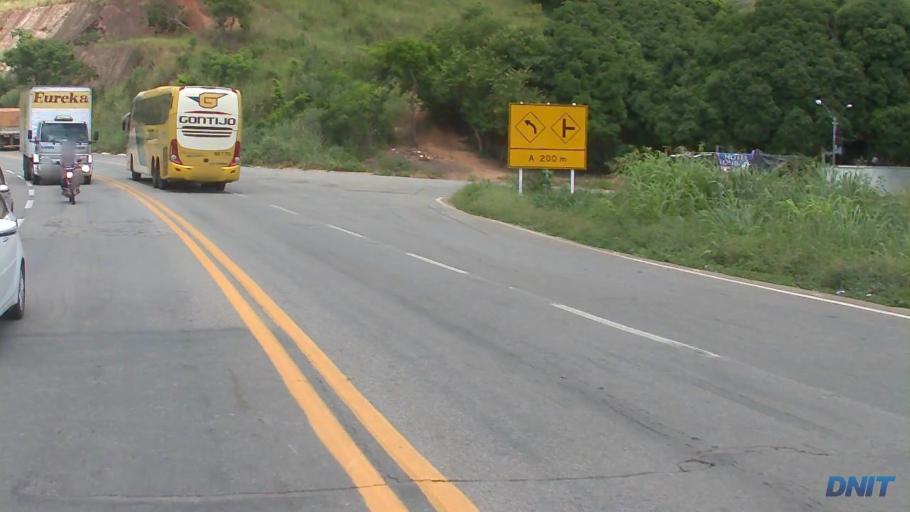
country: BR
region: Minas Gerais
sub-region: Governador Valadares
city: Governador Valadares
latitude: -18.8862
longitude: -41.9989
